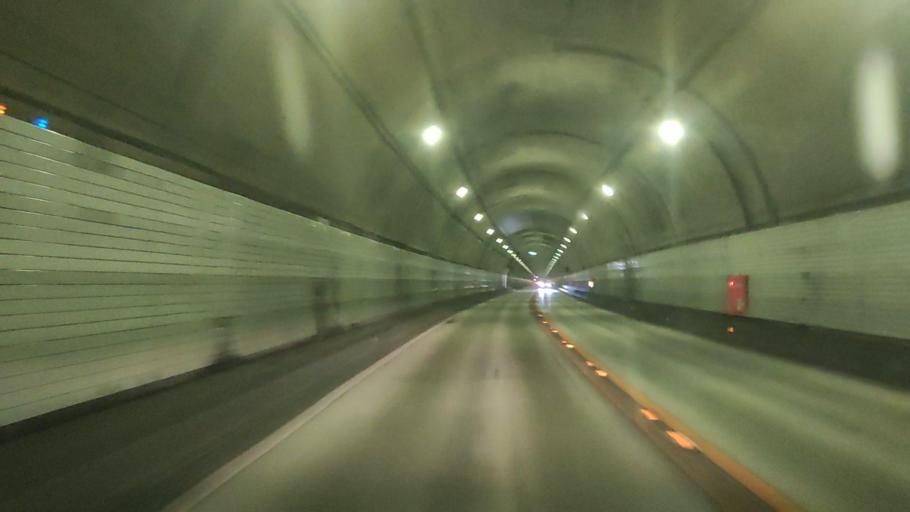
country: JP
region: Fukuoka
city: Maebaru-chuo
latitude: 33.4776
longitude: 130.2880
